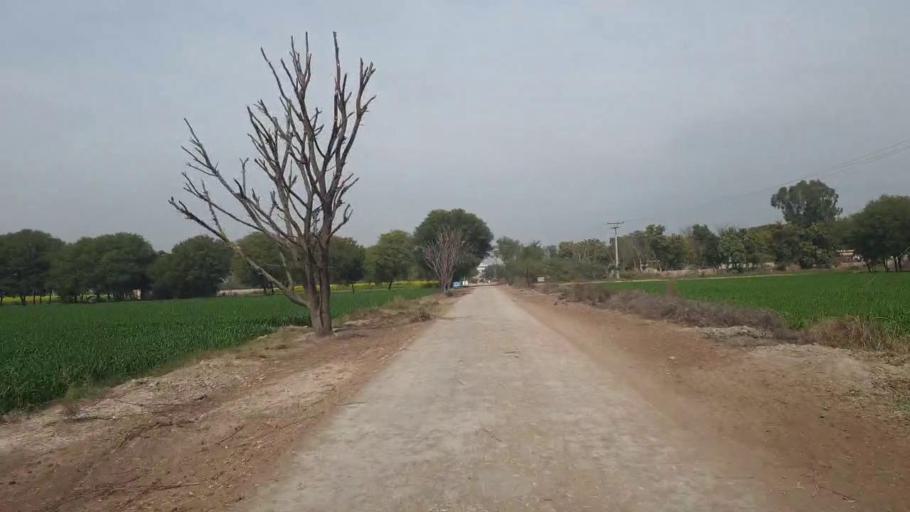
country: PK
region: Sindh
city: Nawabshah
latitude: 26.1215
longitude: 68.4800
